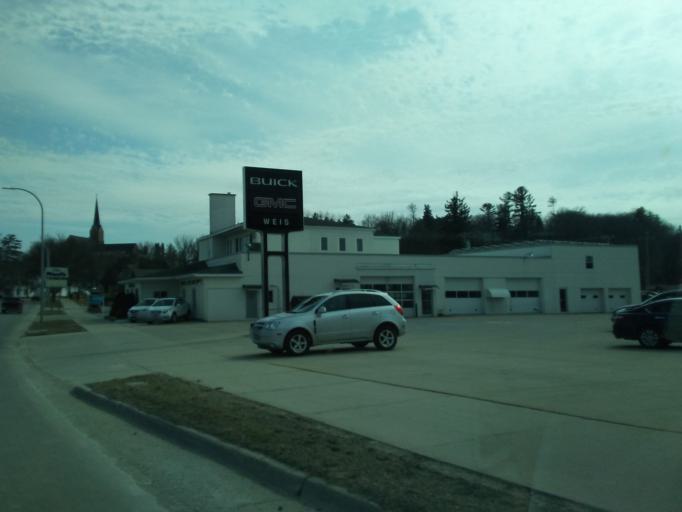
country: US
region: Iowa
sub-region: Winneshiek County
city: Decorah
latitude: 43.3056
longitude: -91.7949
